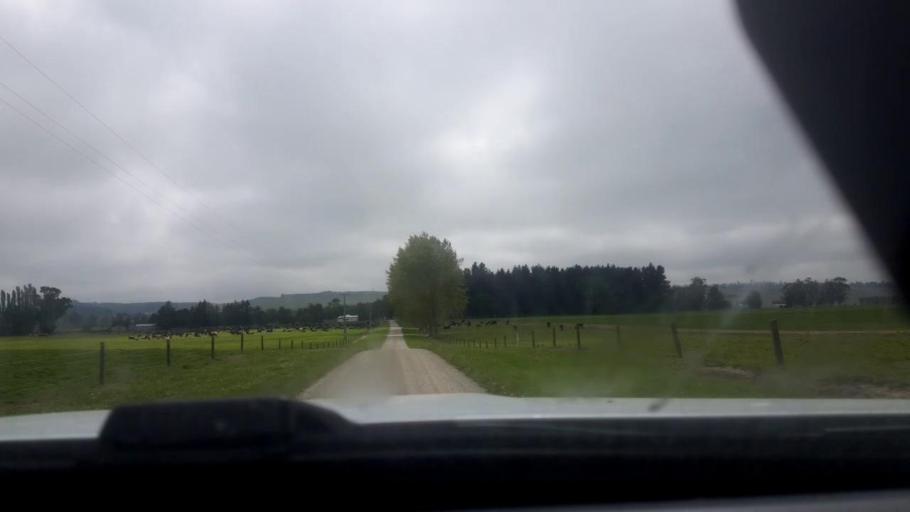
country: NZ
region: Canterbury
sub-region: Timaru District
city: Pleasant Point
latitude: -44.2111
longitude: 171.1102
